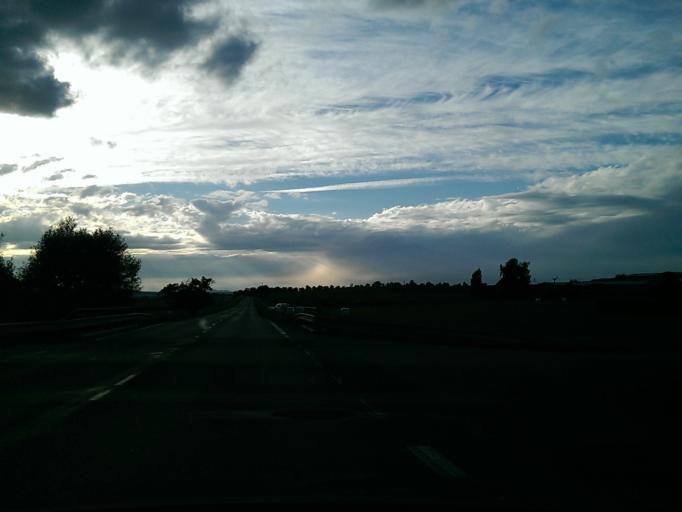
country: CZ
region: Central Bohemia
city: Dolni Bousov
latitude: 50.4644
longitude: 15.1039
